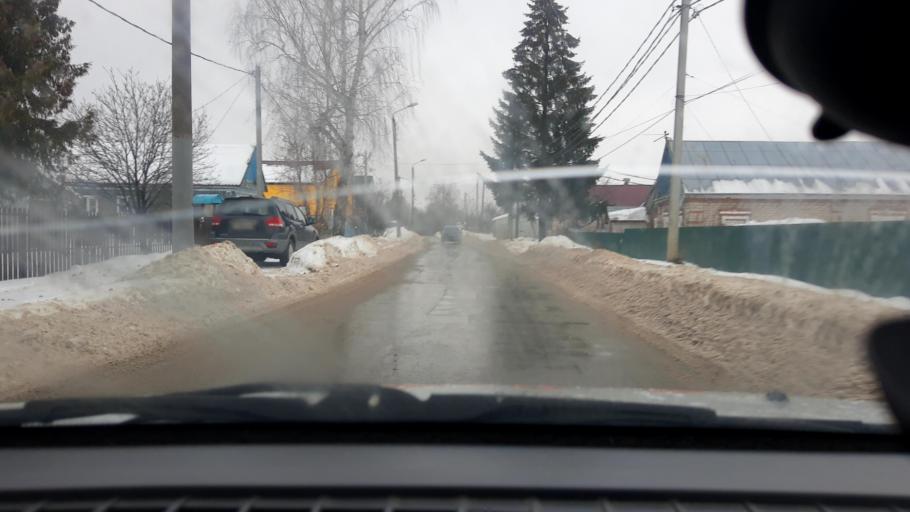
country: RU
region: Nizjnij Novgorod
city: Kstovo
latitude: 56.1903
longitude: 44.1611
